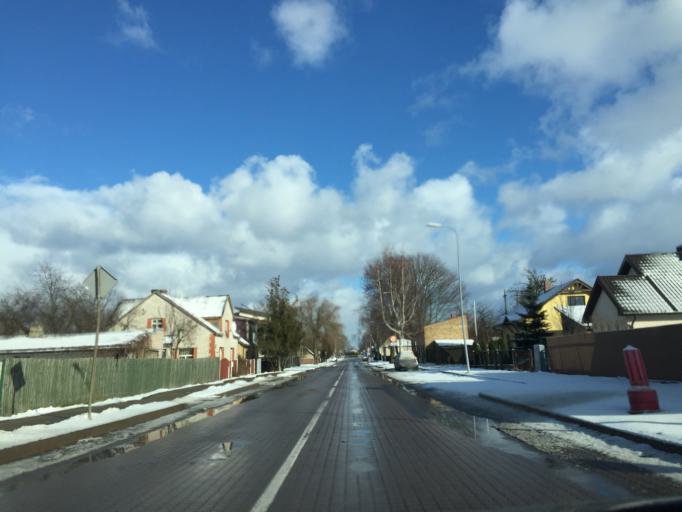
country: LV
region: Ventspils
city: Ventspils
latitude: 57.3822
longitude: 21.5620
